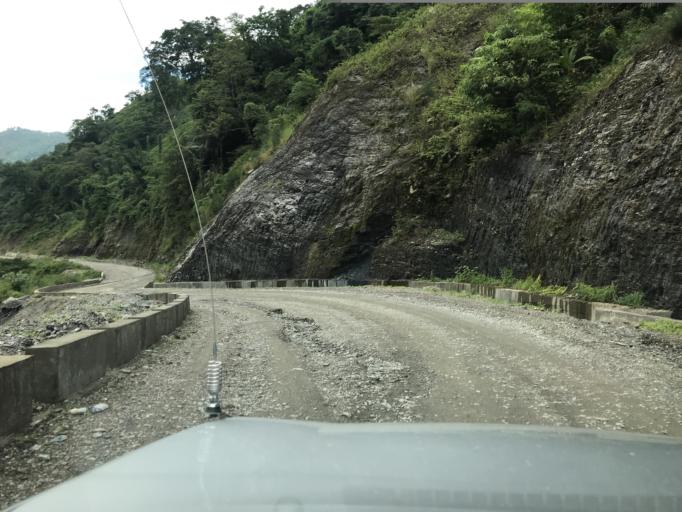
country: TL
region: Aileu
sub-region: Aileu Villa
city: Aileu
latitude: -8.6452
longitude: 125.5231
